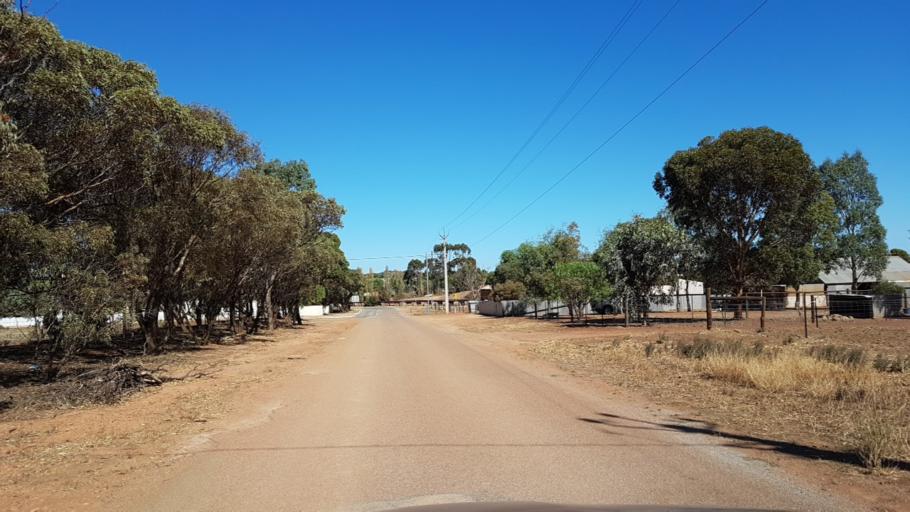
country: AU
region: South Australia
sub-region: Peterborough
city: Peterborough
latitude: -32.9702
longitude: 138.8257
